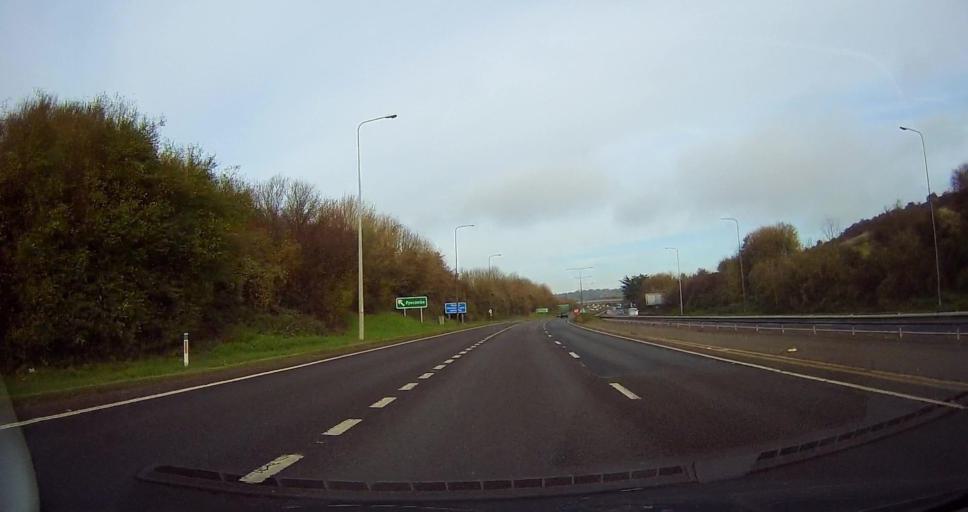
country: GB
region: England
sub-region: West Sussex
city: Hassocks
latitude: 50.8848
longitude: -0.1656
